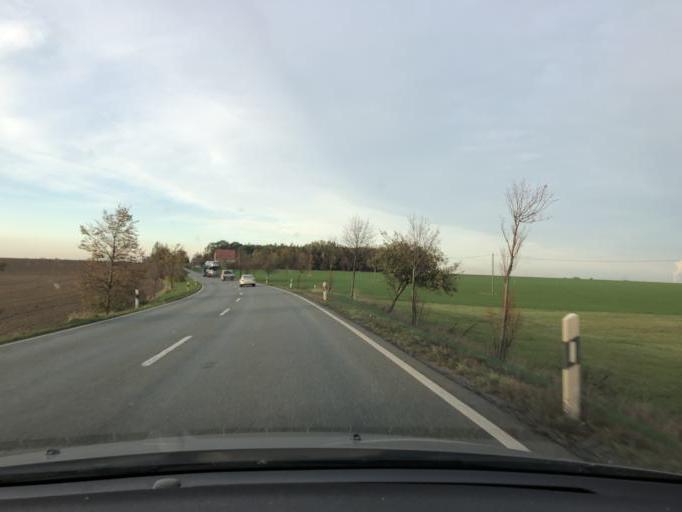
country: DE
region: Thuringia
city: Hirschfeld
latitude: 50.9725
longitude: 12.1354
